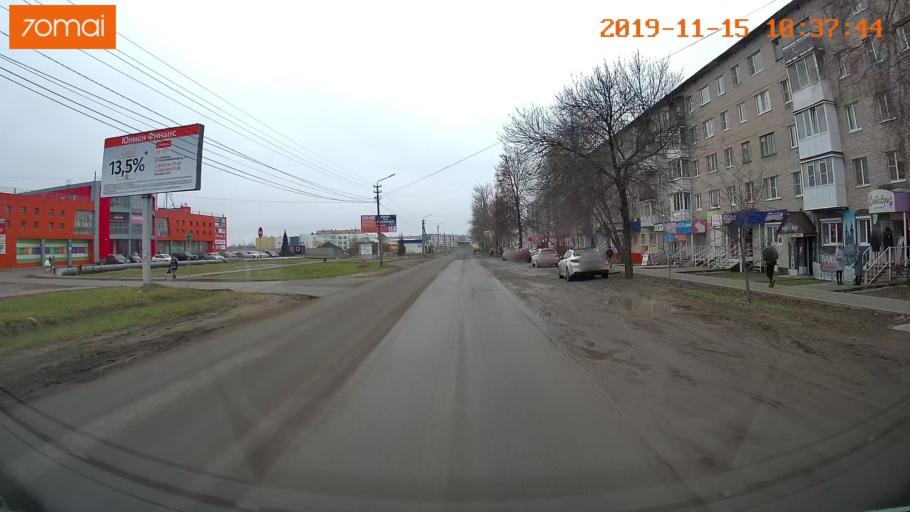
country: RU
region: Vologda
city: Sheksna
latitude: 59.2313
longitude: 38.5130
